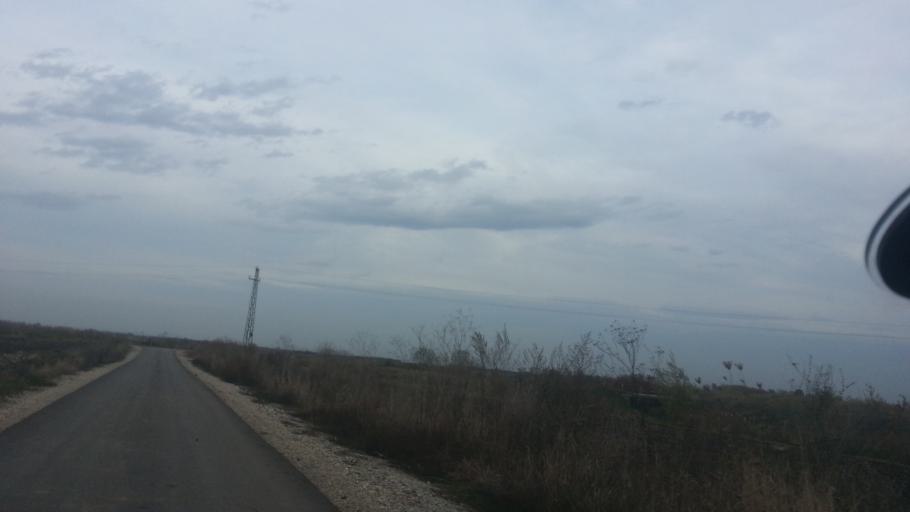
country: RS
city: Putinci
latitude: 44.9729
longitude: 19.9707
